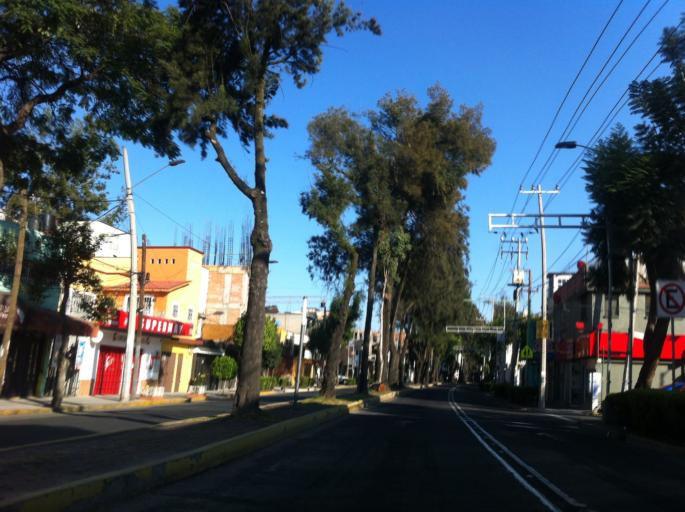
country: MX
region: Mexico City
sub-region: Iztacalco
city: Iztacalco
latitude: 19.4129
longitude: -99.1056
